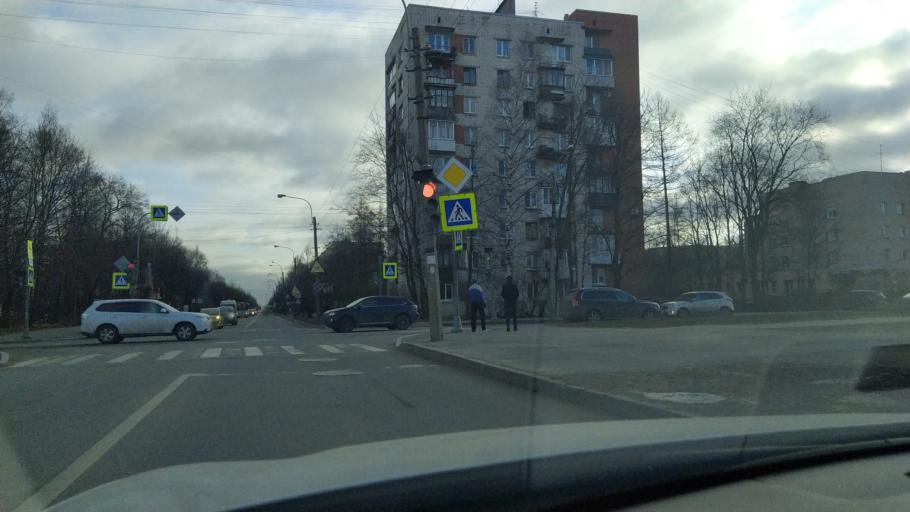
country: RU
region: St.-Petersburg
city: Pushkin
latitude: 59.7305
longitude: 30.4055
